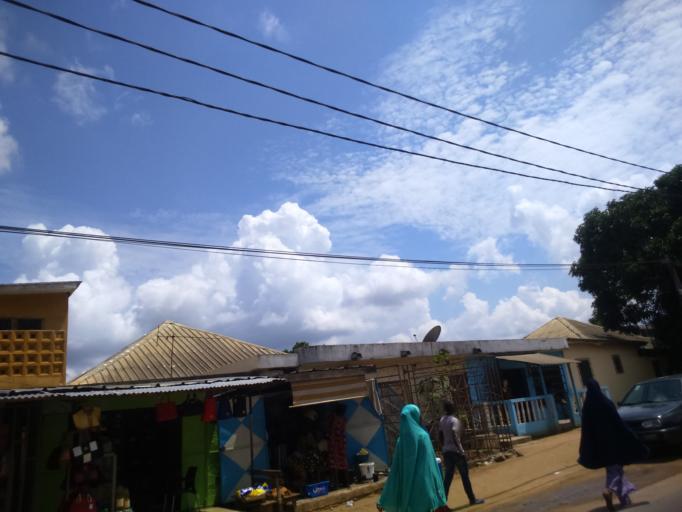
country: CI
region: Lagunes
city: Abidjan
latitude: 5.3418
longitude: -4.0875
